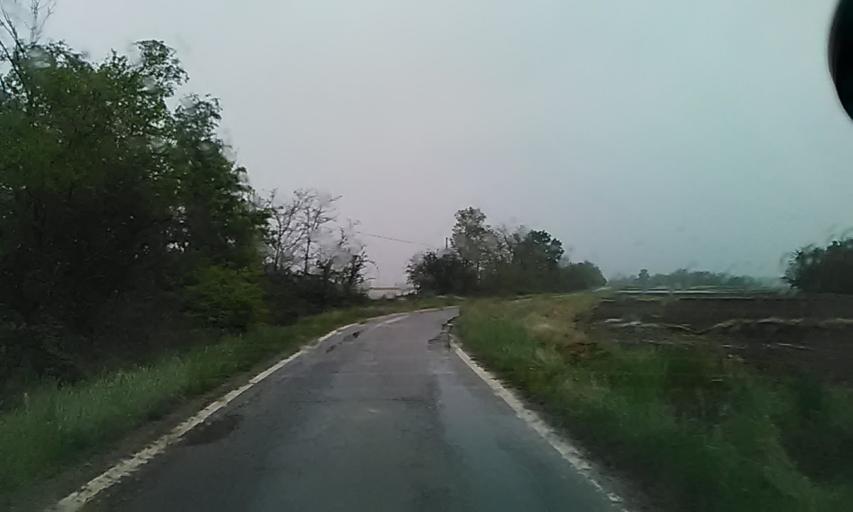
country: IT
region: Piedmont
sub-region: Provincia di Vercelli
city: San Giacomo Vercellese
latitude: 45.4898
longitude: 8.3371
